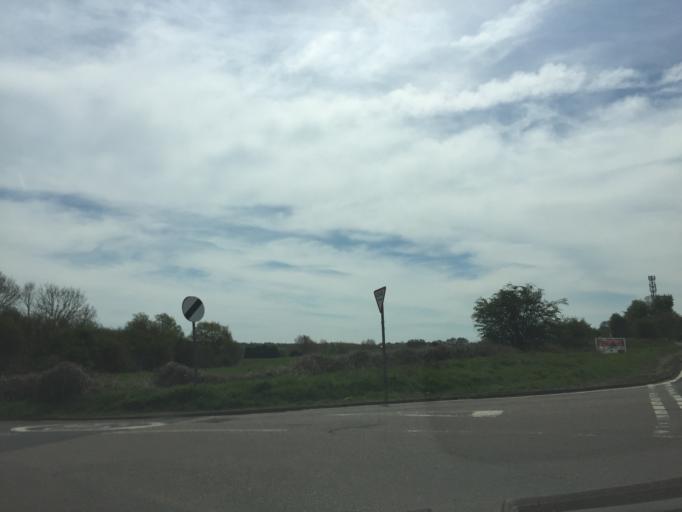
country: GB
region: England
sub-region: Essex
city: Elsenham
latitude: 51.9698
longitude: 0.2162
